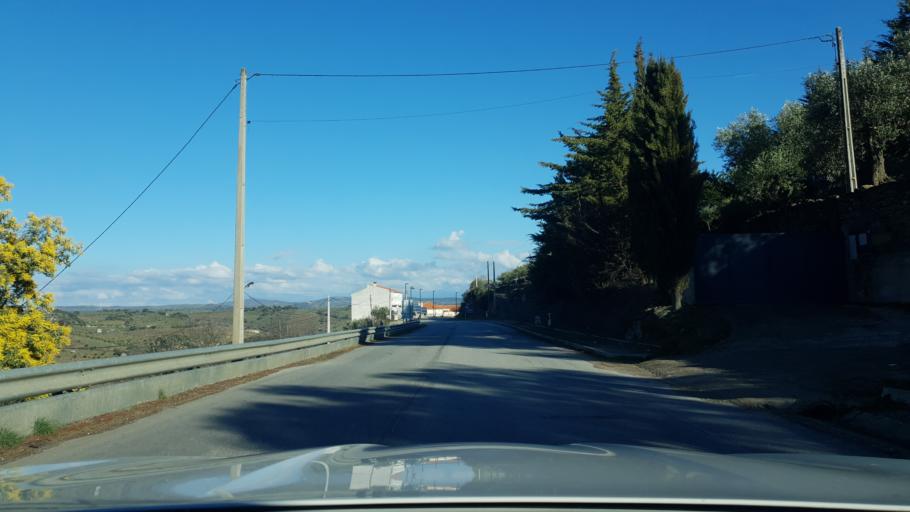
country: PT
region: Braganca
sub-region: Freixo de Espada A Cinta
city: Freixo de Espada a Cinta
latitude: 41.0951
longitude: -6.8164
